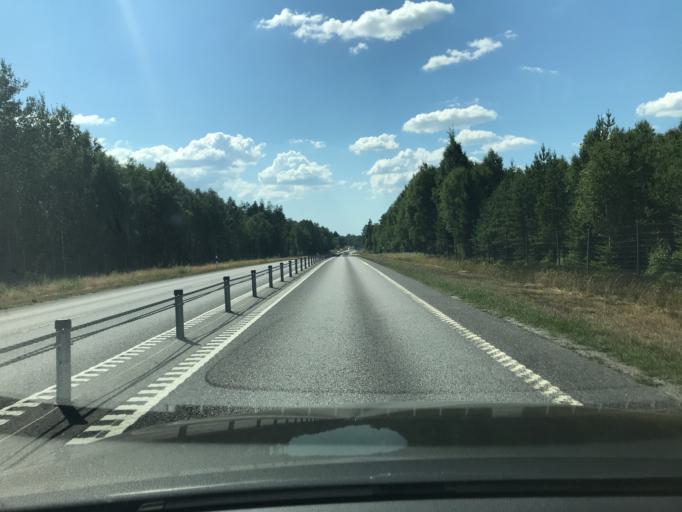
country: SE
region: Kronoberg
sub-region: Alvesta Kommun
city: Vislanda
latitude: 56.7009
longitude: 14.3648
